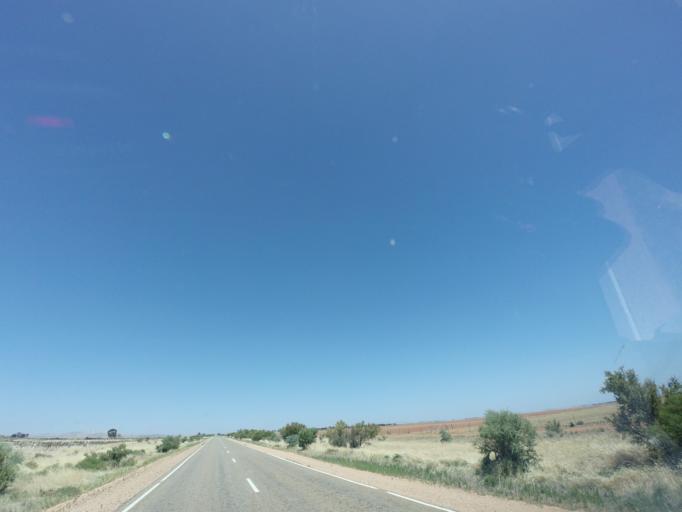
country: AU
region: South Australia
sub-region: Flinders Ranges
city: Quorn
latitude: -32.6709
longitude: 138.2549
